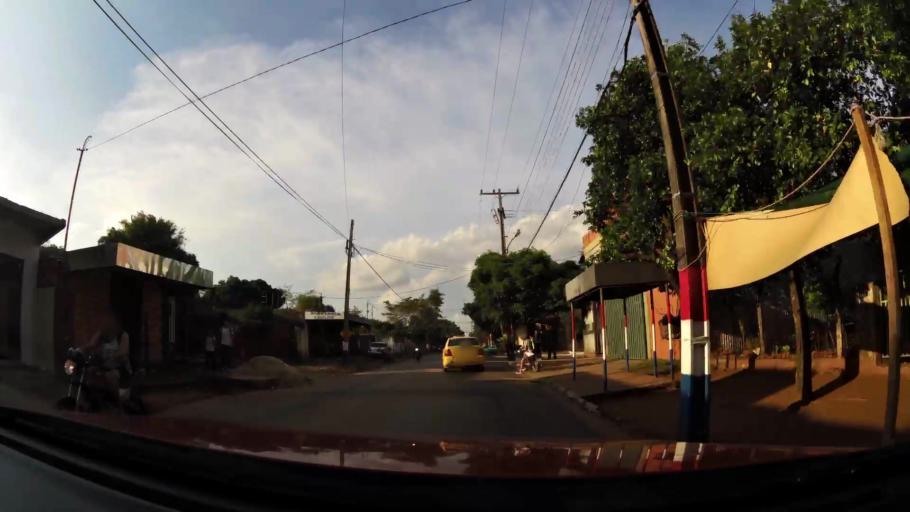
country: PY
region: Central
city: Fernando de la Mora
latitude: -25.3636
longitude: -57.5302
